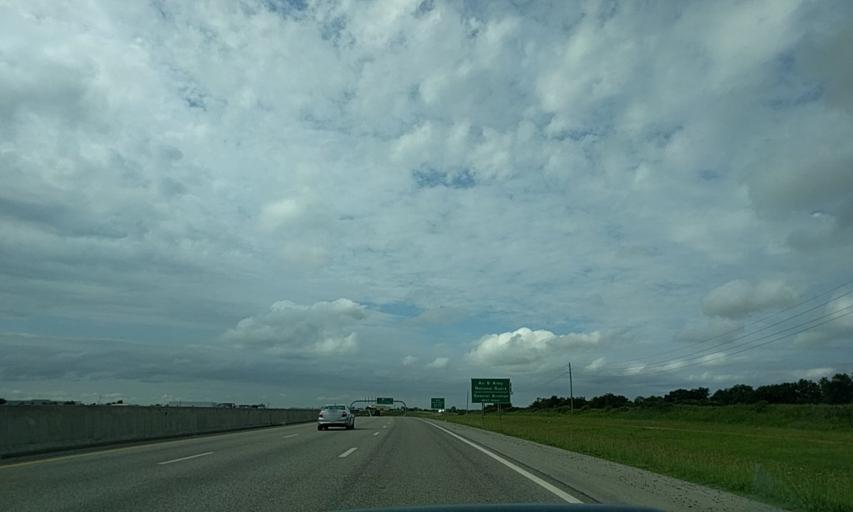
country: US
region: Oklahoma
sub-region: Tulsa County
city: Owasso
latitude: 36.2267
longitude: -95.8512
